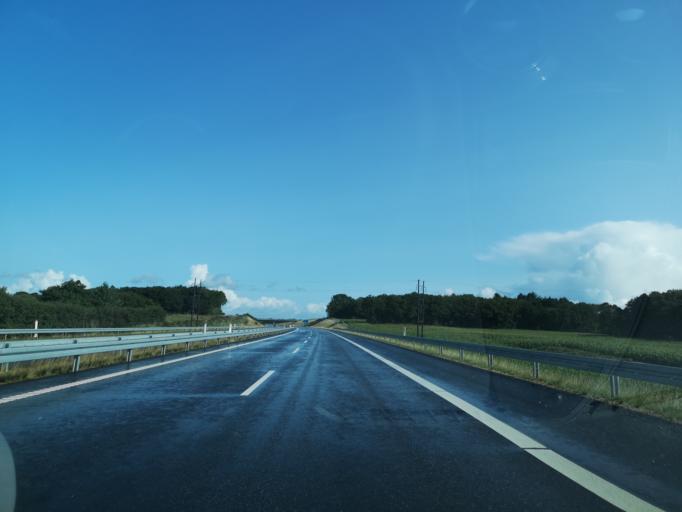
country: DK
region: Central Jutland
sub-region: Herning Kommune
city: Snejbjerg
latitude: 56.1691
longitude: 8.8898
